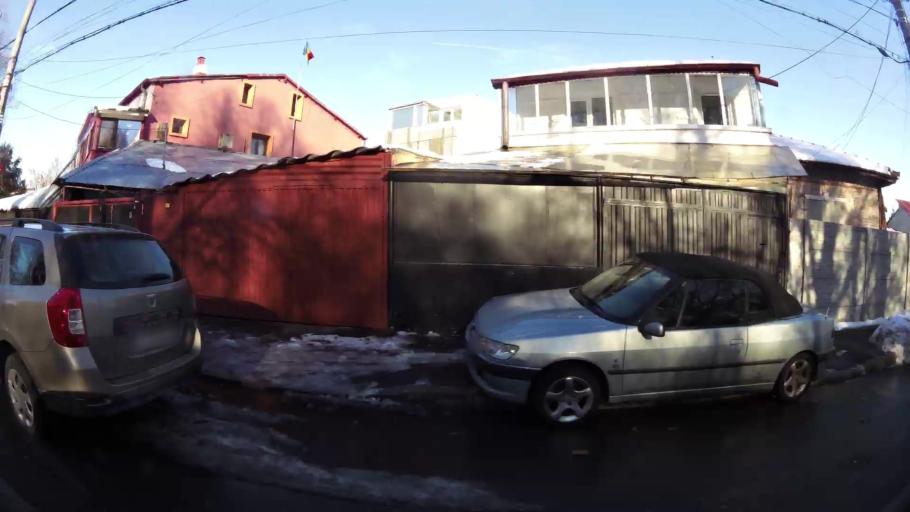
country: RO
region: Ilfov
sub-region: Comuna Fundeni-Dobroesti
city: Fundeni
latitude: 44.4661
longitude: 26.1319
